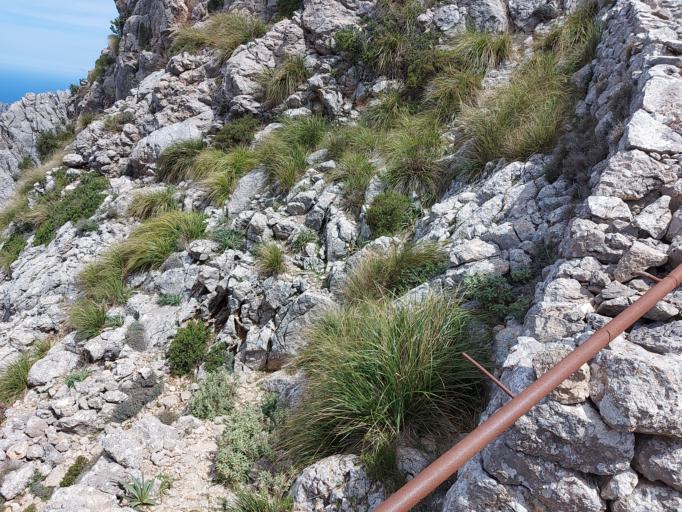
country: ES
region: Balearic Islands
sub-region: Illes Balears
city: Fornalutx
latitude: 39.7743
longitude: 2.7596
